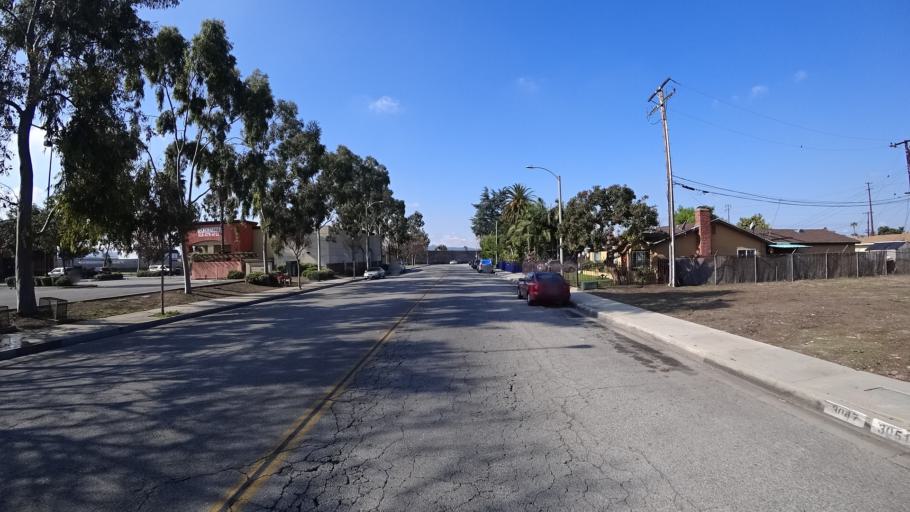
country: US
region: California
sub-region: Los Angeles County
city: Baldwin Park
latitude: 34.0708
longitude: -117.9657
